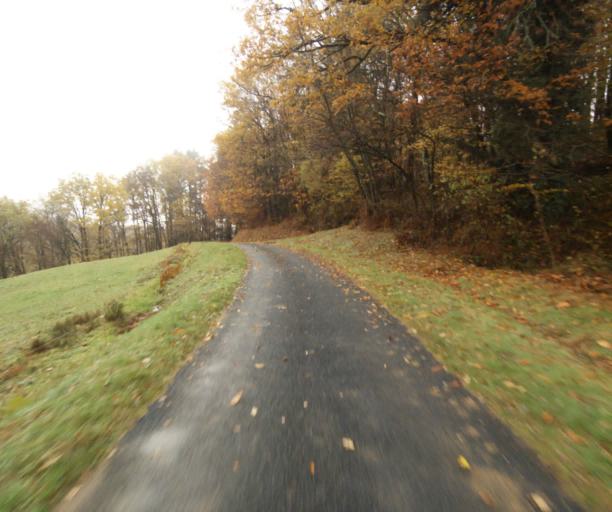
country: FR
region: Limousin
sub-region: Departement de la Correze
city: Cornil
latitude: 45.1954
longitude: 1.6346
